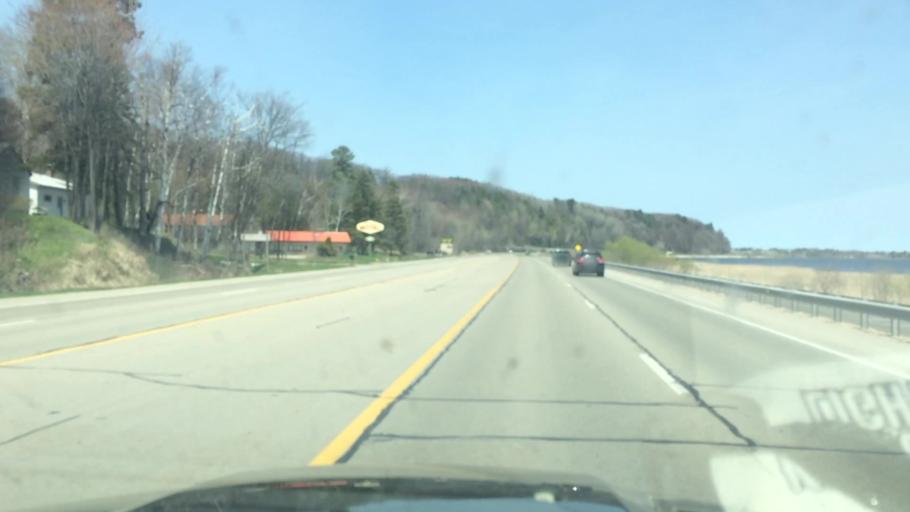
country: US
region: Michigan
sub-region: Delta County
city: Gladstone
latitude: 45.8173
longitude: -87.0556
